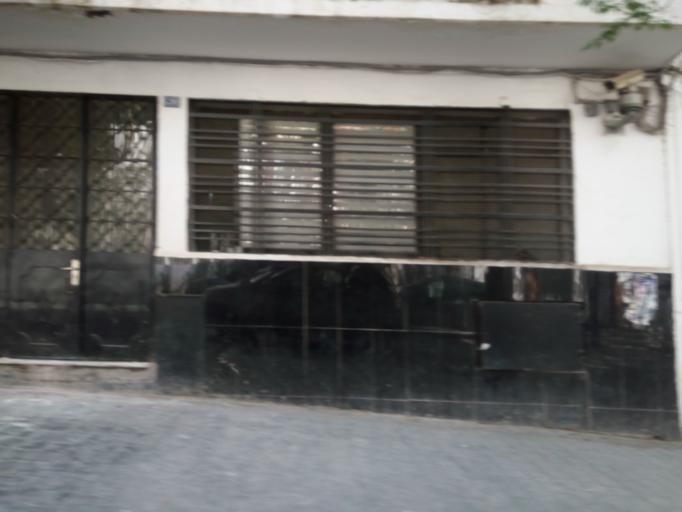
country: DZ
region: Constantine
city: Constantine
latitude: 36.3614
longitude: 6.6051
